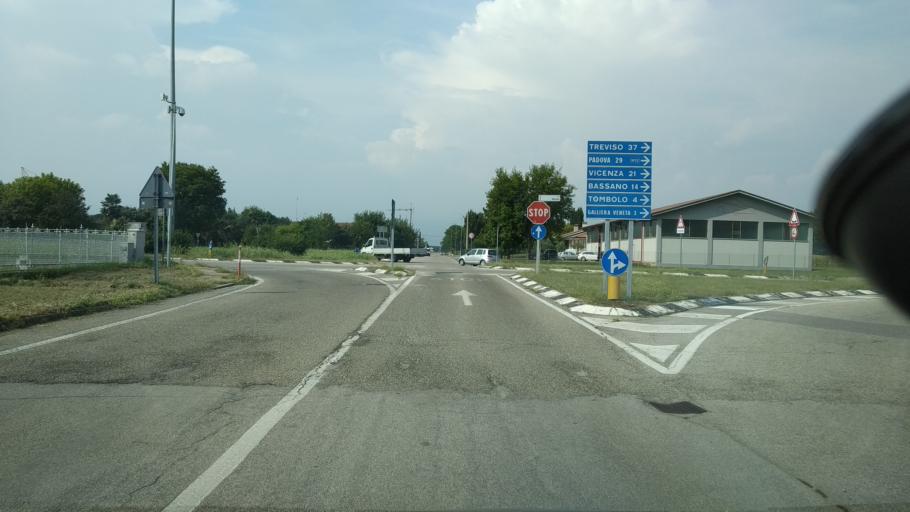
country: IT
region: Veneto
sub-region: Provincia di Padova
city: Cittadella
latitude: 45.6545
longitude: 11.7899
